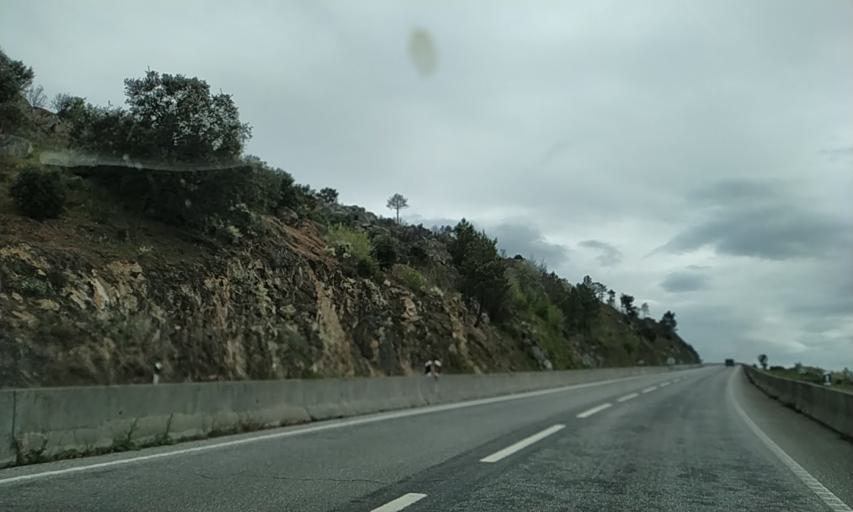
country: PT
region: Guarda
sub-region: Guarda
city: Guarda
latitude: 40.6006
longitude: -7.2750
